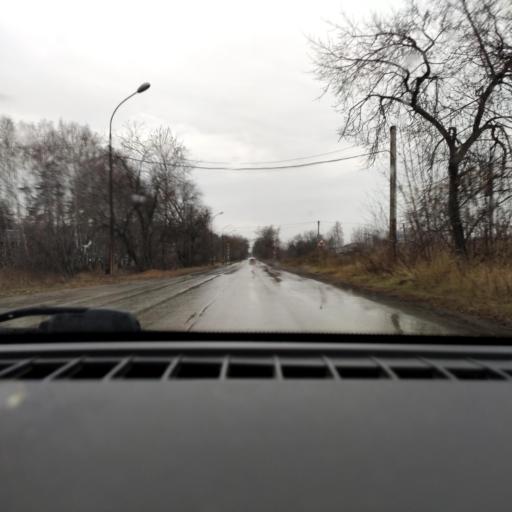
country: RU
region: Perm
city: Kultayevo
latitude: 57.9931
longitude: 55.9221
